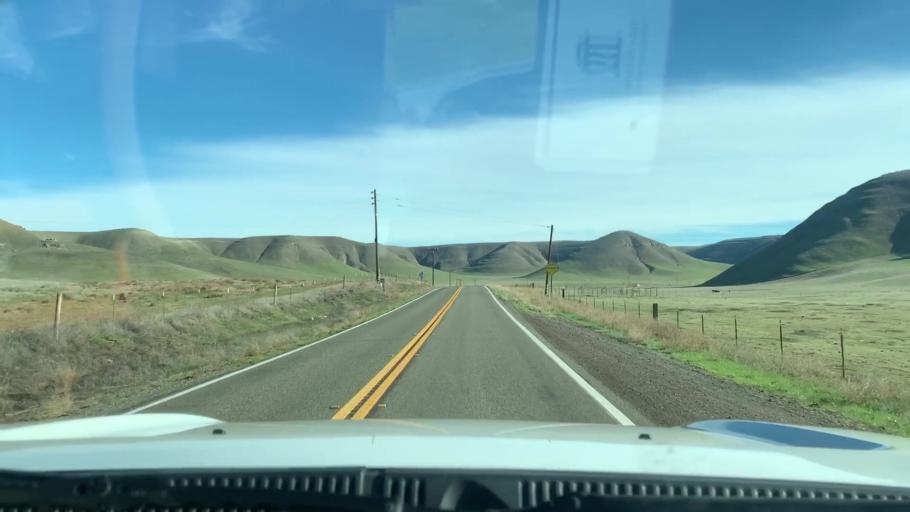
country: US
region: California
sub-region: Monterey County
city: King City
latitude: 36.1540
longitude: -120.9957
